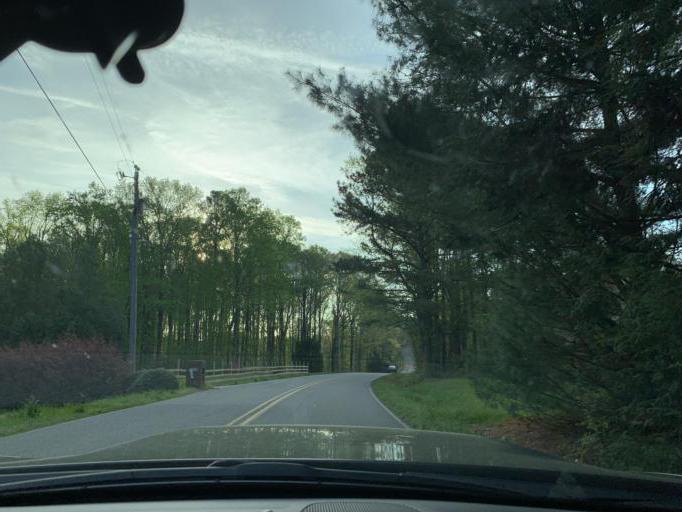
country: US
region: Georgia
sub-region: Forsyth County
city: Cumming
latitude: 34.2596
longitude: -84.1515
